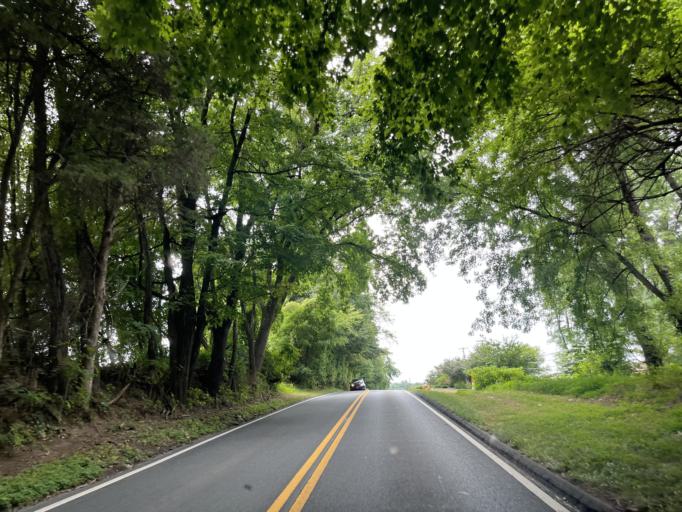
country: US
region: Maryland
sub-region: Montgomery County
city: Montgomery Village
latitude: 39.2266
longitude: -77.1772
